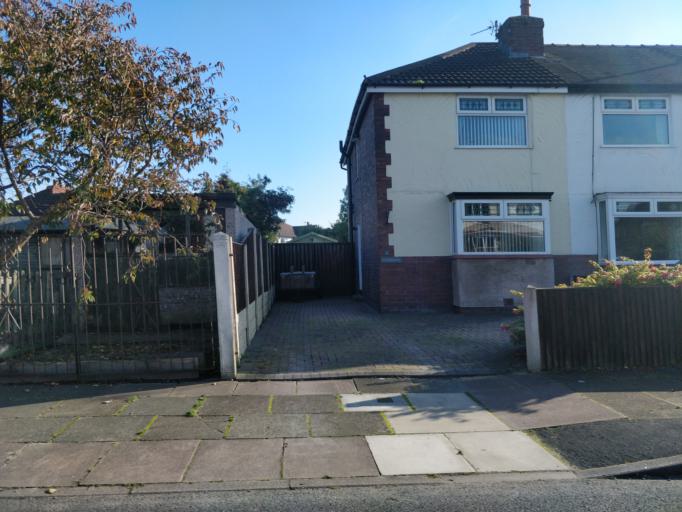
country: GB
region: England
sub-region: Lancashire
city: Banks
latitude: 53.6717
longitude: -2.9533
